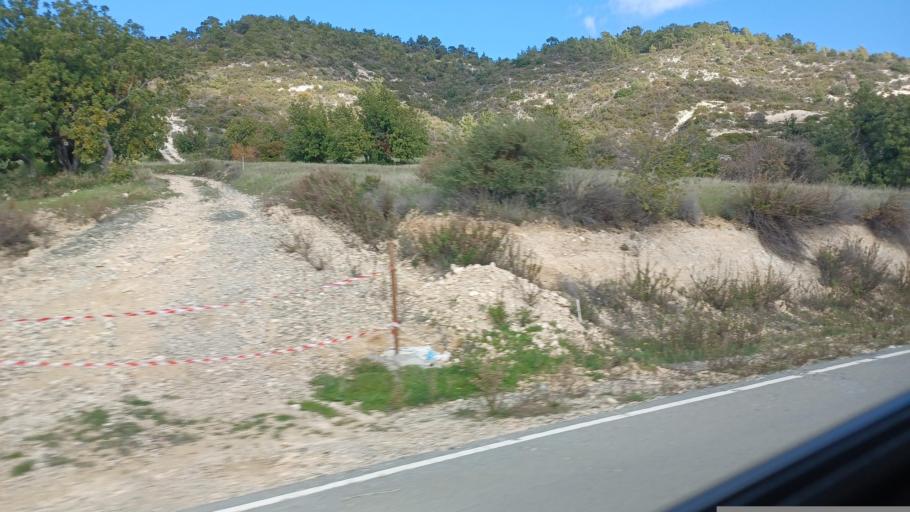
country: CY
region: Limassol
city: Pano Polemidia
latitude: 34.7938
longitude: 32.9794
